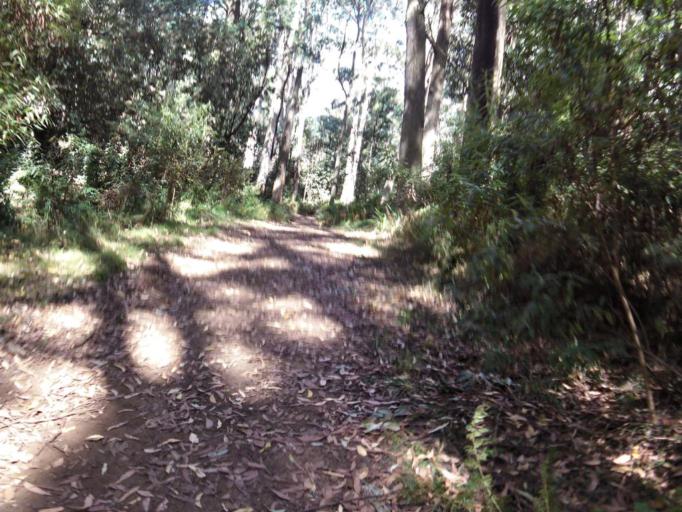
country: AU
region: Victoria
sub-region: Hume
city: Sunbury
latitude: -37.3676
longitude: 144.5989
